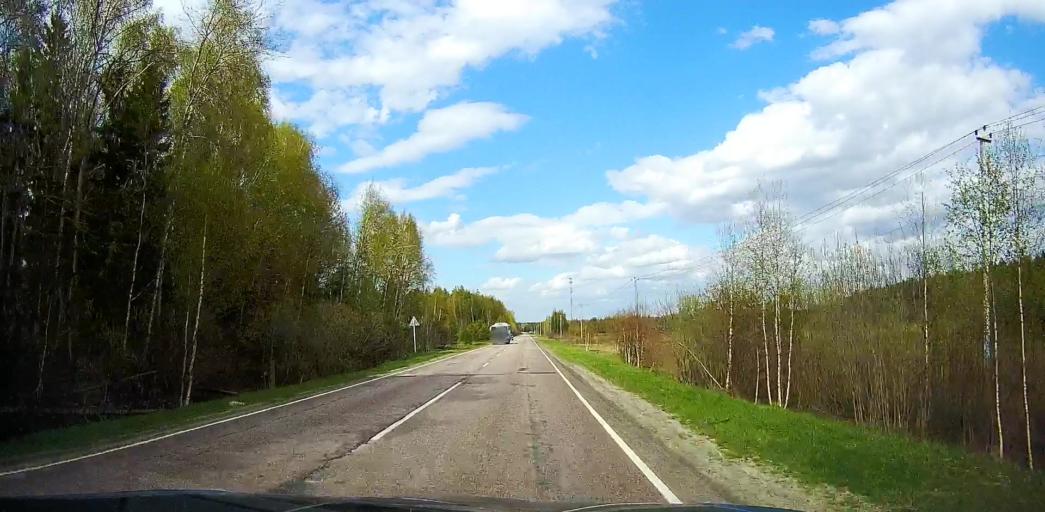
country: RU
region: Moskovskaya
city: Rakhmanovo
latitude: 55.6628
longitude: 38.6401
